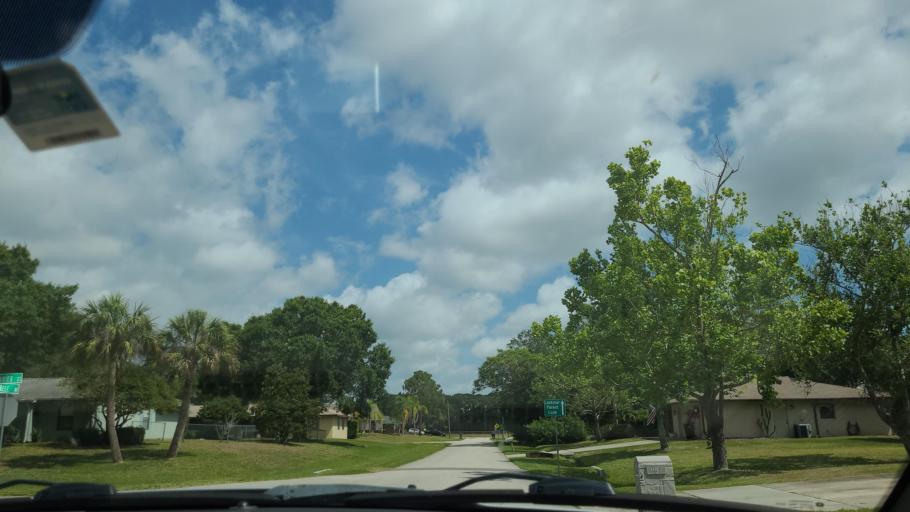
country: US
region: Florida
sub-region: Brevard County
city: West Melbourne
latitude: 28.0228
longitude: -80.6571
